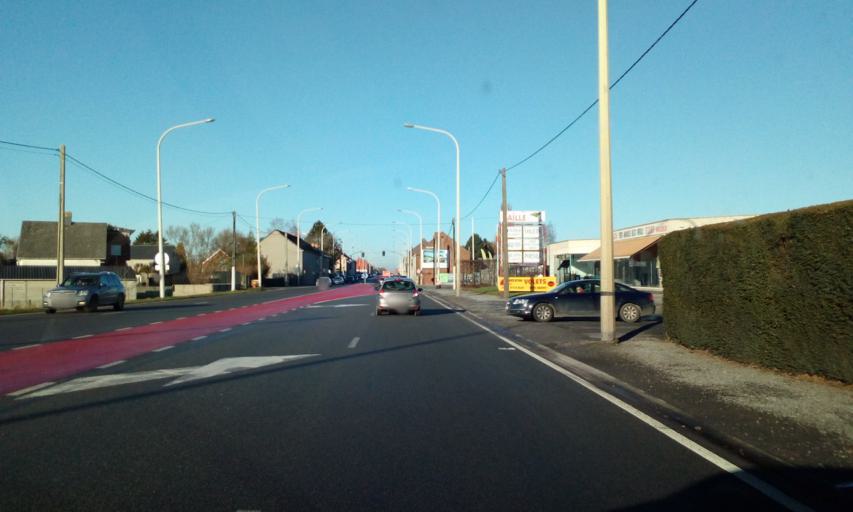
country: BE
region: Wallonia
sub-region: Province du Hainaut
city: Gerpinnes
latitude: 50.3359
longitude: 4.4747
